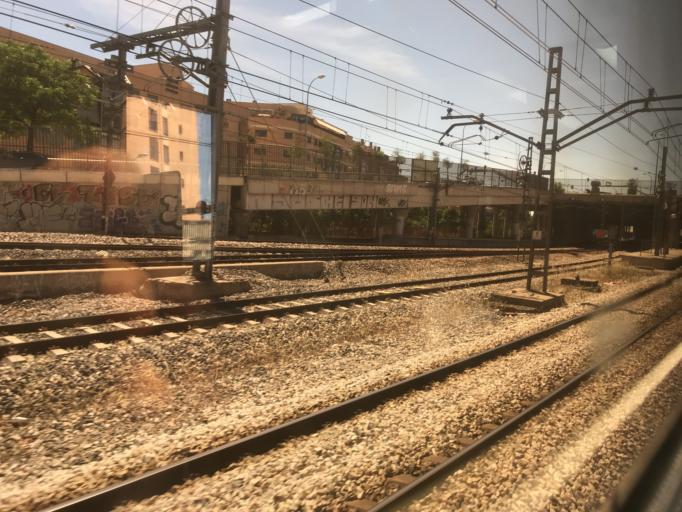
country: ES
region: Madrid
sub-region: Provincia de Madrid
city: Villaverde
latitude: 40.3561
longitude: -3.6837
